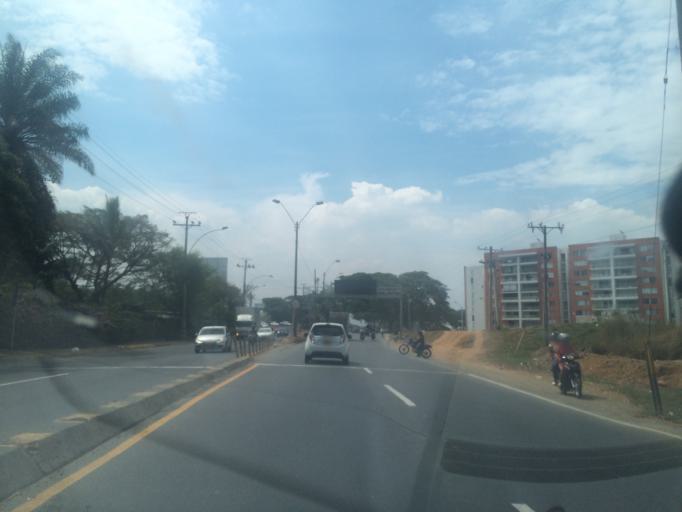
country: CO
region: Valle del Cauca
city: Cali
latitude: 3.3619
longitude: -76.5245
